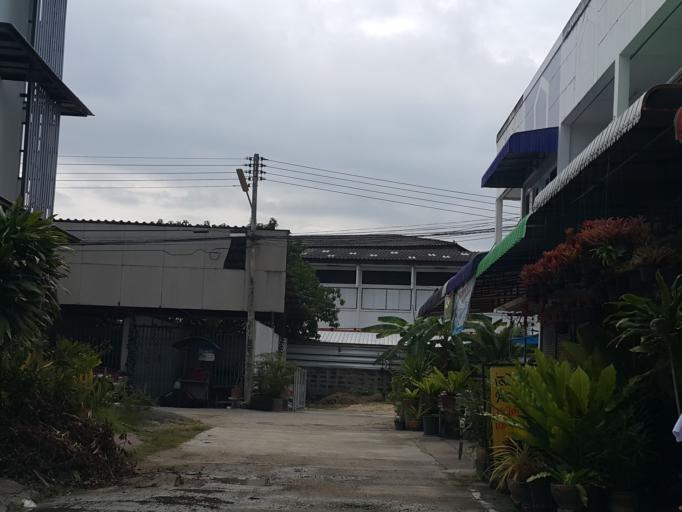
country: TH
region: Lampang
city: Lampang
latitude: 18.2992
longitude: 99.4974
